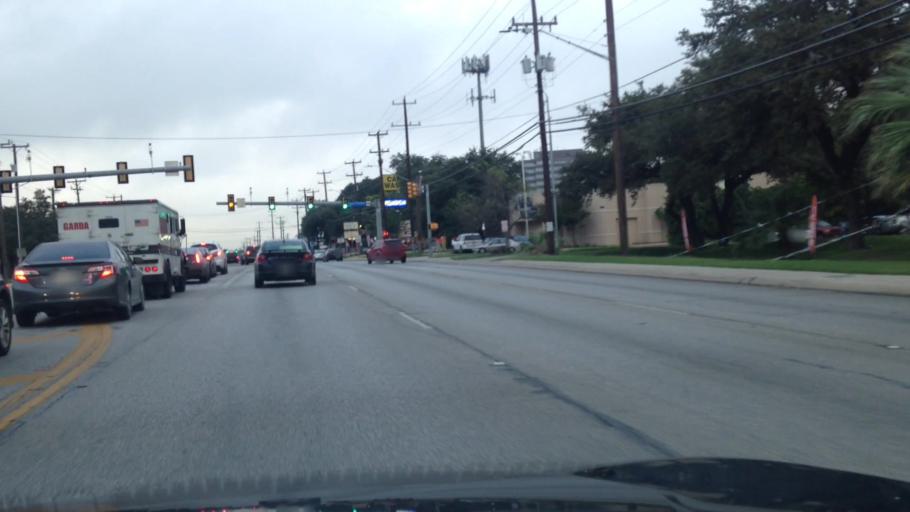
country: US
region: Texas
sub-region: Bexar County
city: Balcones Heights
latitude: 29.5103
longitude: -98.5667
